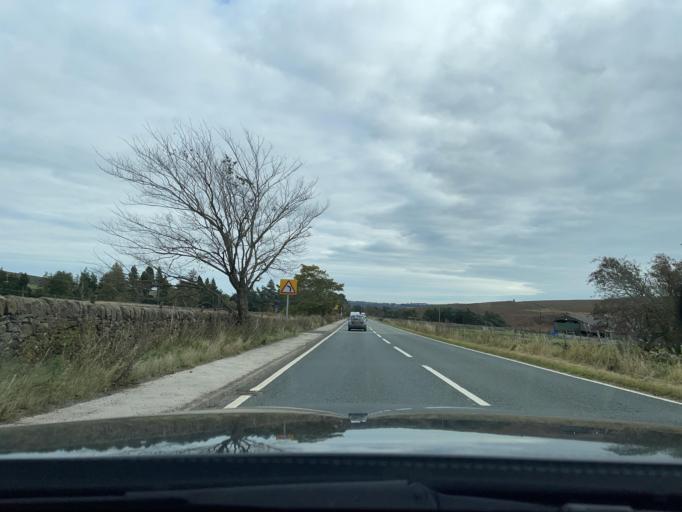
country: GB
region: England
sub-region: Sheffield
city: Bradfield
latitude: 53.3867
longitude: -1.6269
